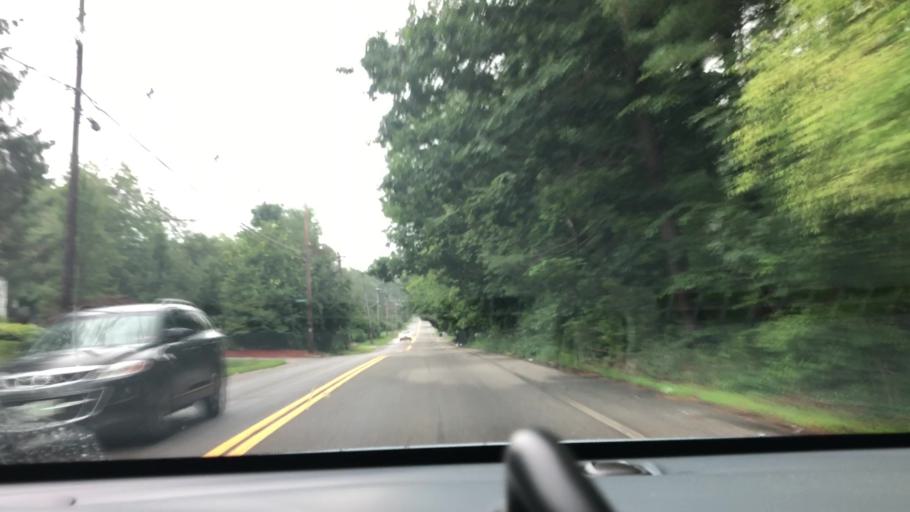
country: US
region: New Hampshire
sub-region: Merrimack County
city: South Hooksett
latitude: 43.0282
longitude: -71.4626
